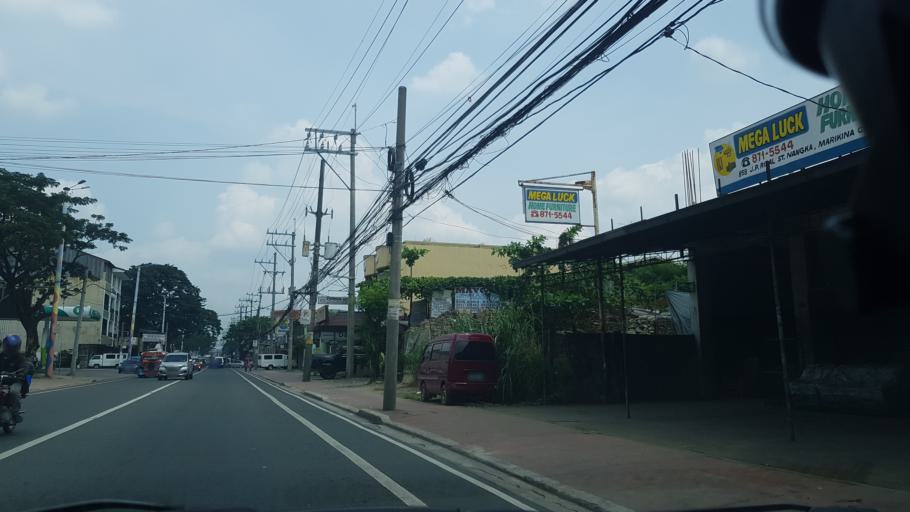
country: PH
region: Calabarzon
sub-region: Province of Rizal
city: San Mateo
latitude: 14.6680
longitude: 121.1078
